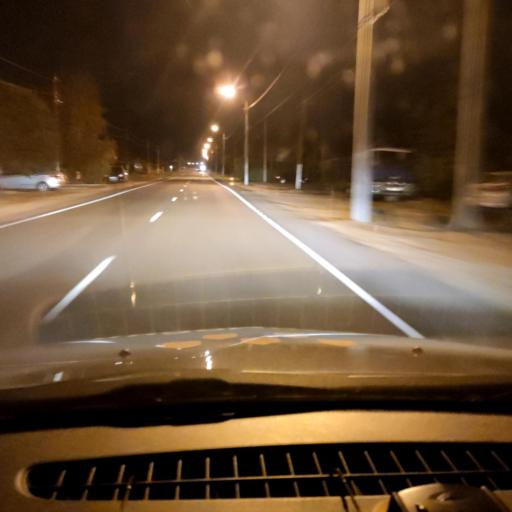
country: RU
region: Voronezj
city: Shilovo
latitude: 51.5764
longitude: 39.0387
